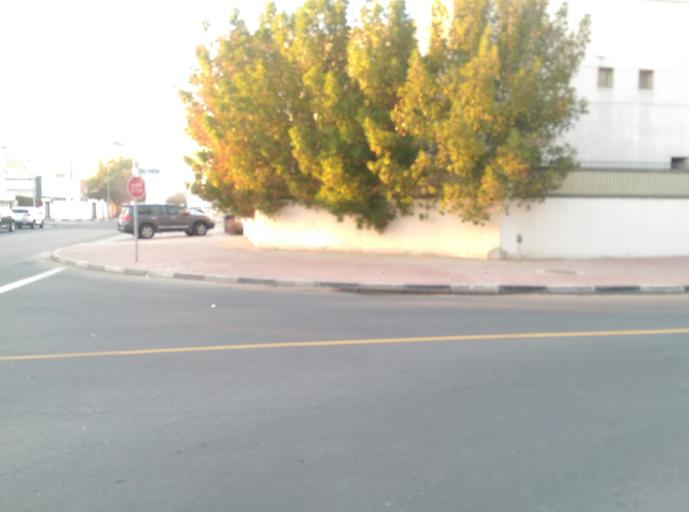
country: AE
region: Ash Shariqah
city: Sharjah
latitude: 25.2297
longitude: 55.2638
